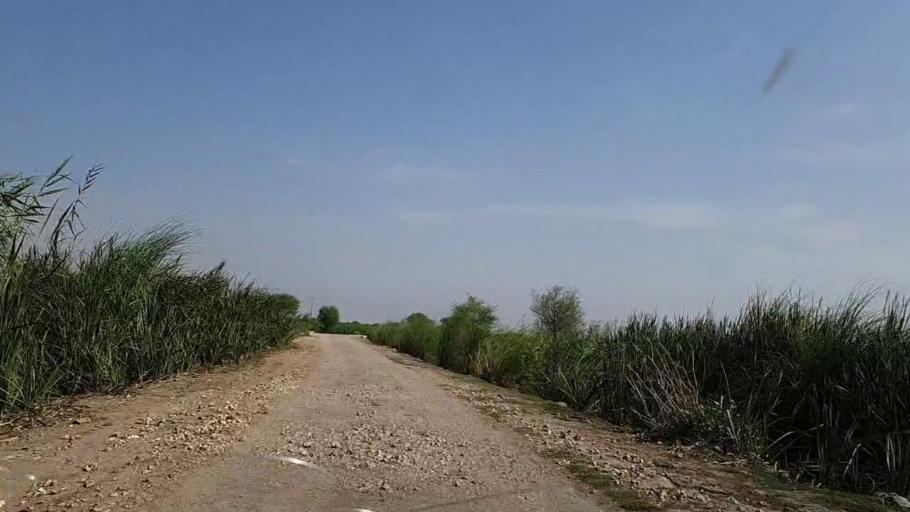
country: PK
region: Sindh
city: Khanpur
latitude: 27.7163
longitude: 69.3619
